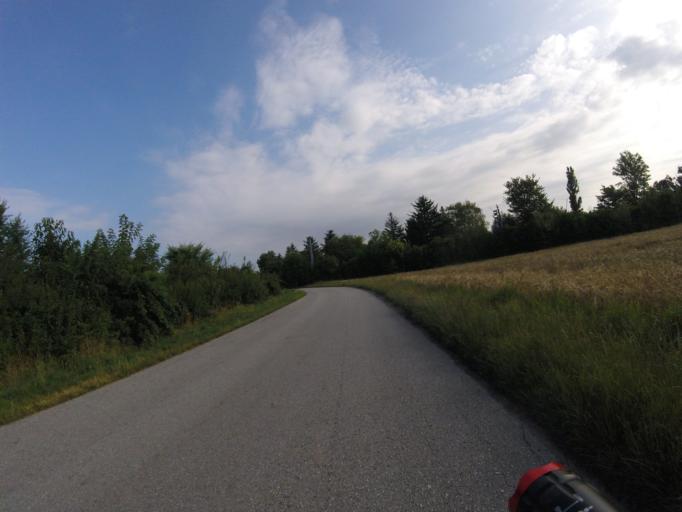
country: AT
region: Lower Austria
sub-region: Politischer Bezirk Baden
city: Trumau
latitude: 48.0292
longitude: 16.3466
